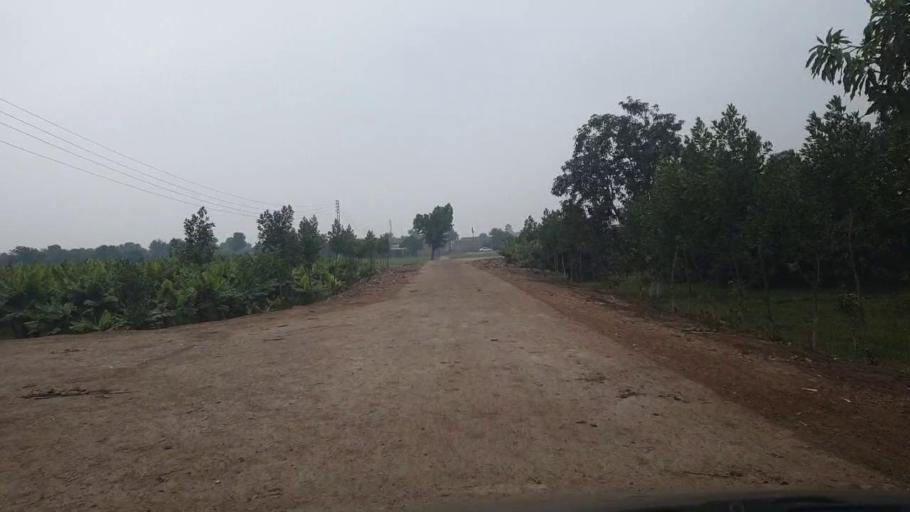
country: PK
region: Sindh
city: Tando Adam
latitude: 25.8036
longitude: 68.6674
